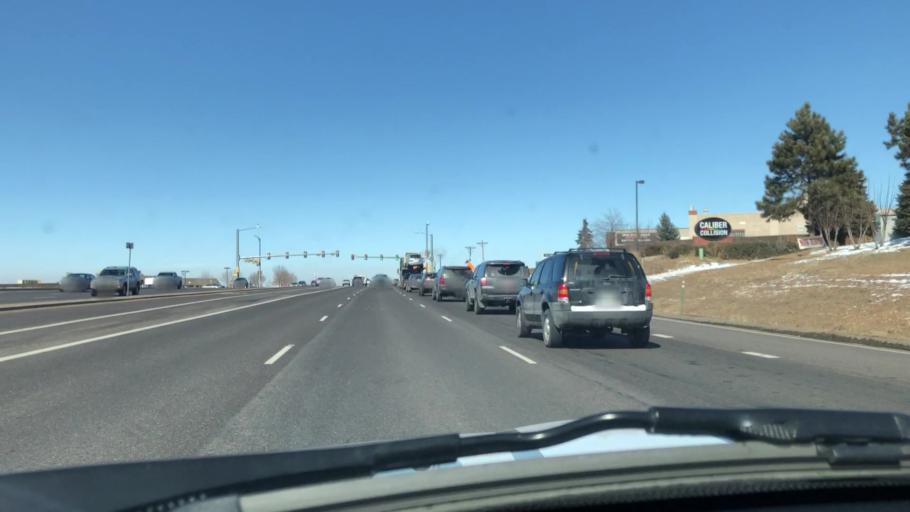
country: US
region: Colorado
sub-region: Douglas County
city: Parker
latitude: 39.5426
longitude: -104.7710
